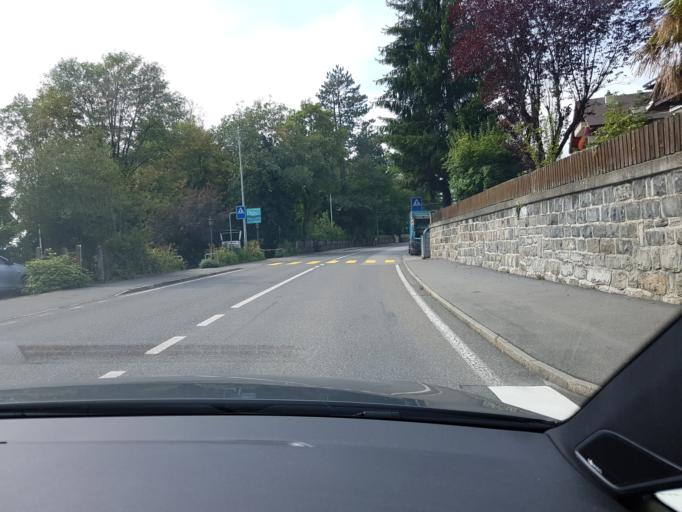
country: CH
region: Bern
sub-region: Thun District
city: Sigriswil
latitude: 46.6949
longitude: 7.7407
